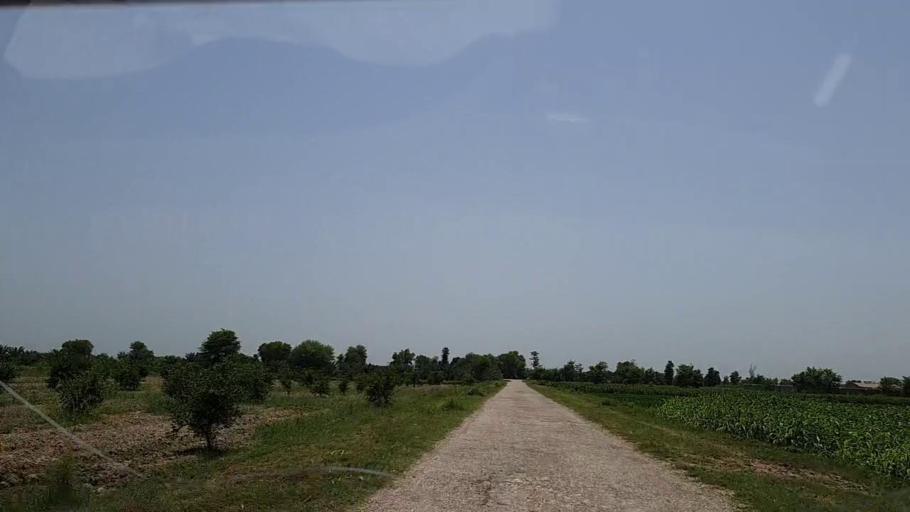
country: PK
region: Sindh
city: Tharu Shah
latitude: 26.9211
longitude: 68.0458
